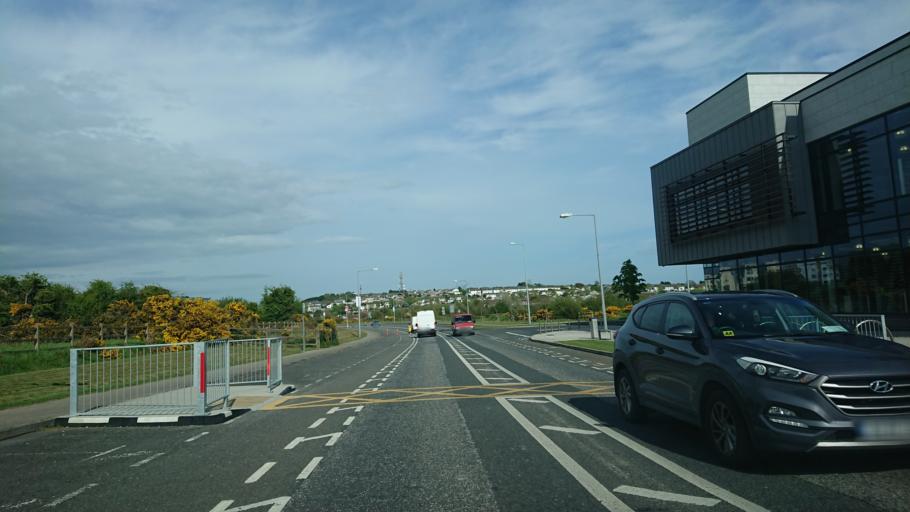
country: IE
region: Munster
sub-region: Waterford
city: Waterford
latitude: 52.2612
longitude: -7.1472
